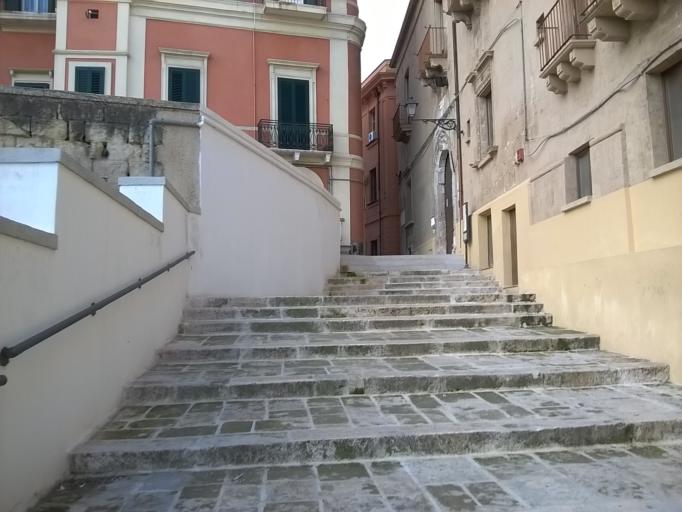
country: IT
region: Apulia
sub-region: Provincia di Taranto
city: Taranto
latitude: 40.4743
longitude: 17.2344
